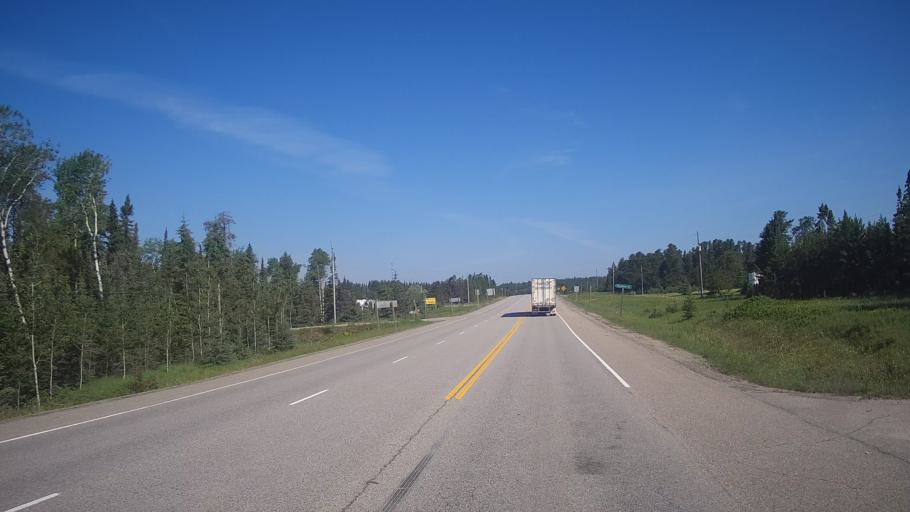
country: CA
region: Ontario
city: Dryden
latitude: 49.7133
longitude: -92.5918
